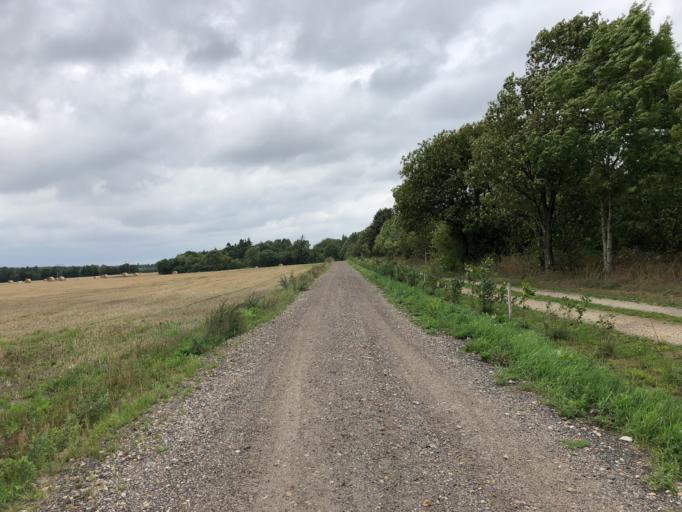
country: DK
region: Central Jutland
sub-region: Herning Kommune
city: Lind
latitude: 56.0639
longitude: 8.9853
